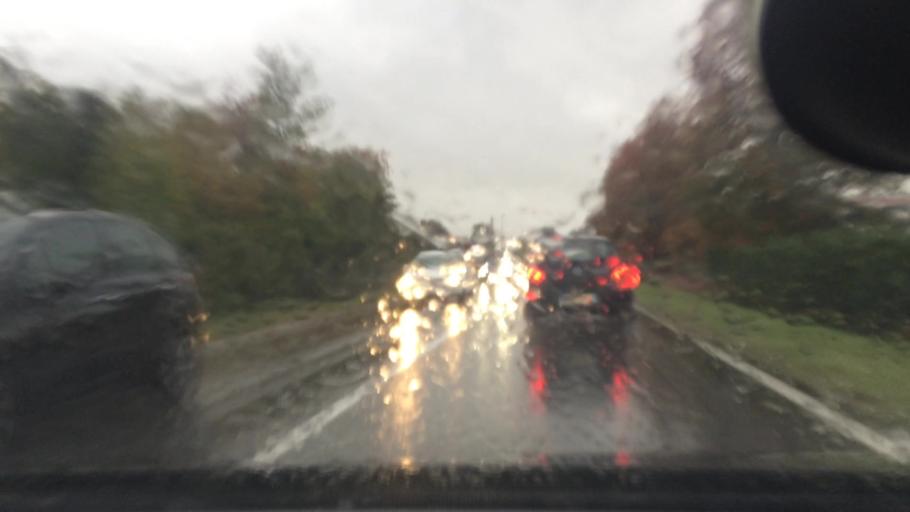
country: IT
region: Lombardy
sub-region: Citta metropolitana di Milano
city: Parabiago
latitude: 45.5464
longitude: 8.9533
